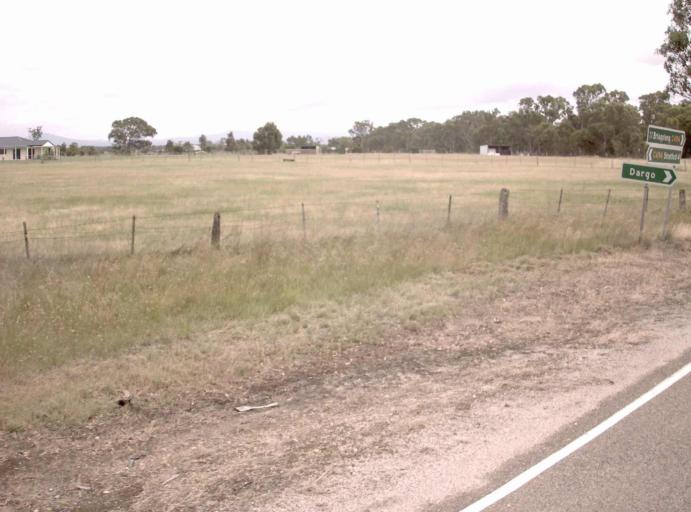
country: AU
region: Victoria
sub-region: Wellington
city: Sale
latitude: -37.9343
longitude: 147.0962
